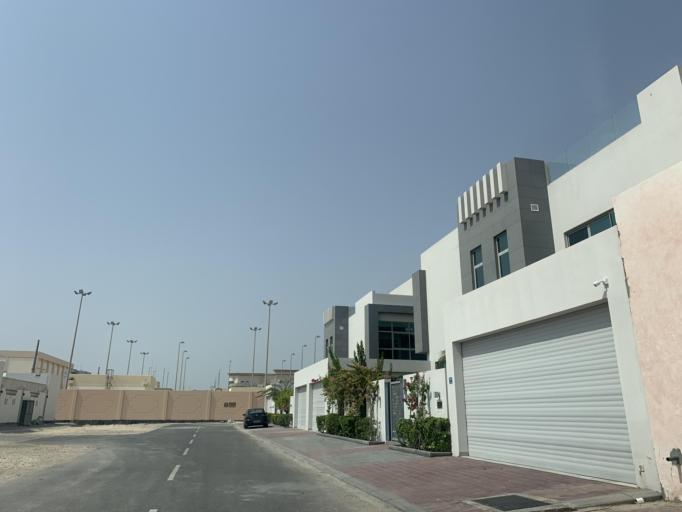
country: BH
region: Central Governorate
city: Madinat Hamad
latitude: 26.1652
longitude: 50.4808
